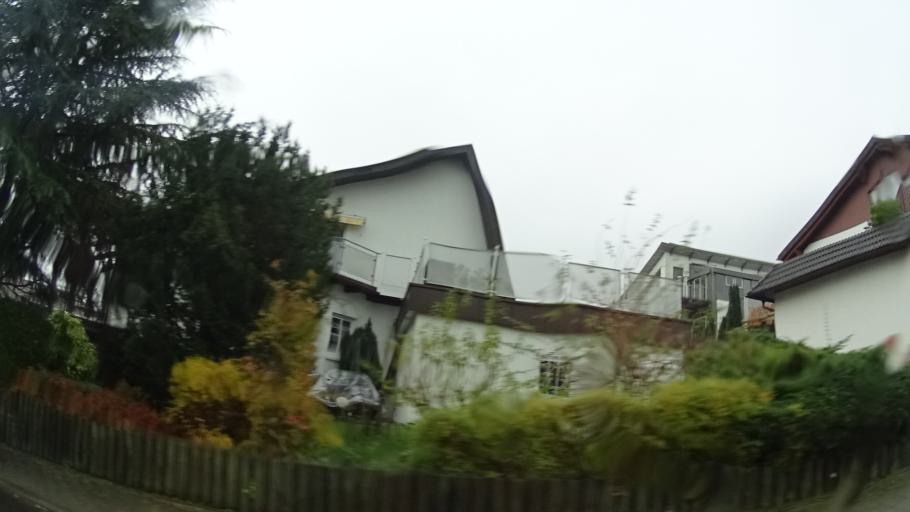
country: DE
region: Baden-Wuerttemberg
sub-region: Karlsruhe Region
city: Sinzheim
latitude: 48.7544
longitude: 8.1809
